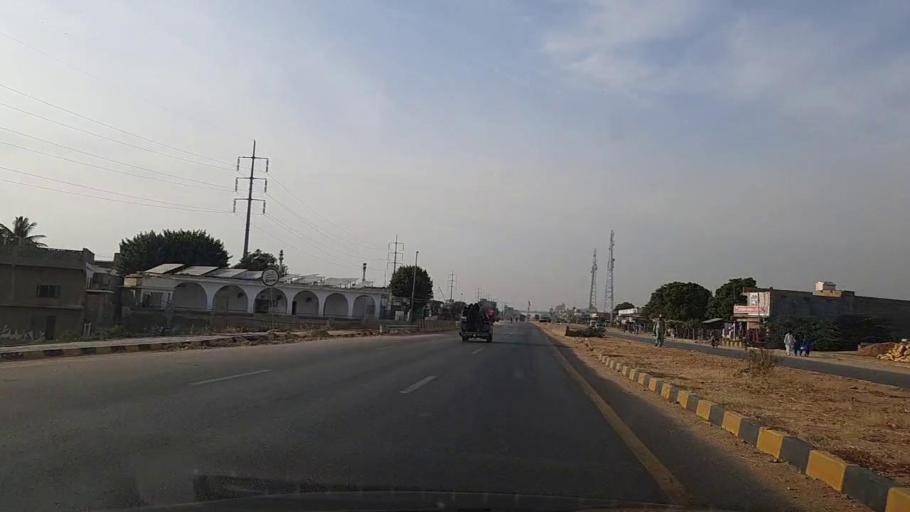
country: PK
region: Sindh
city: Gharo
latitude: 24.7863
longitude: 67.5303
